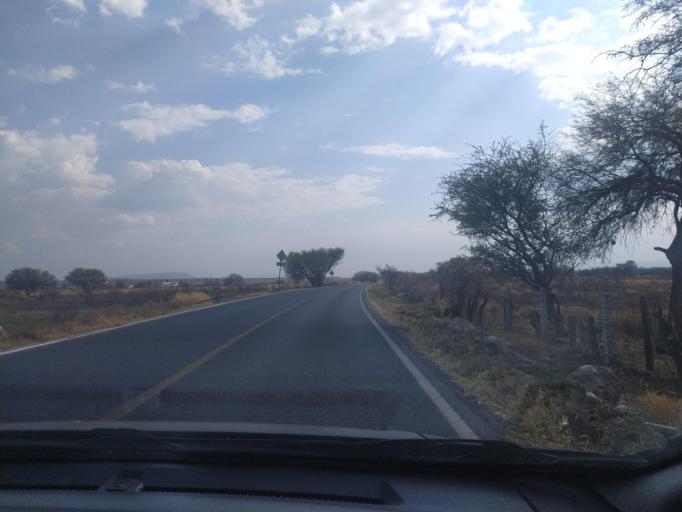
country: MX
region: Guanajuato
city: San Roque
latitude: 20.9676
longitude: -101.8456
